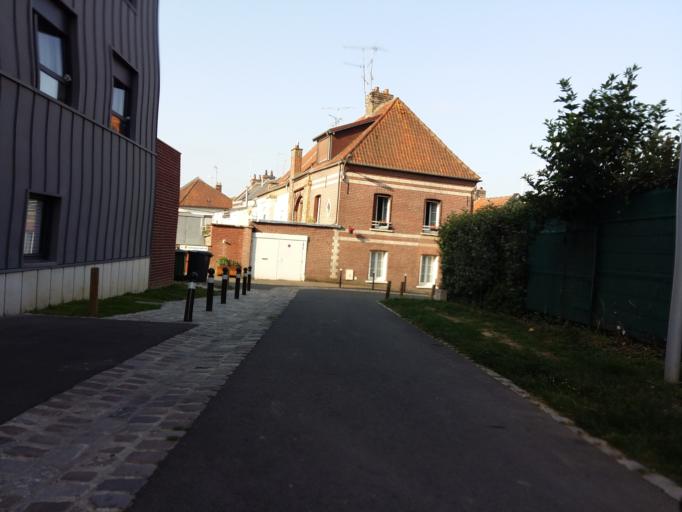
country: FR
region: Picardie
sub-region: Departement de la Somme
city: Amiens
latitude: 49.9025
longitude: 2.2889
